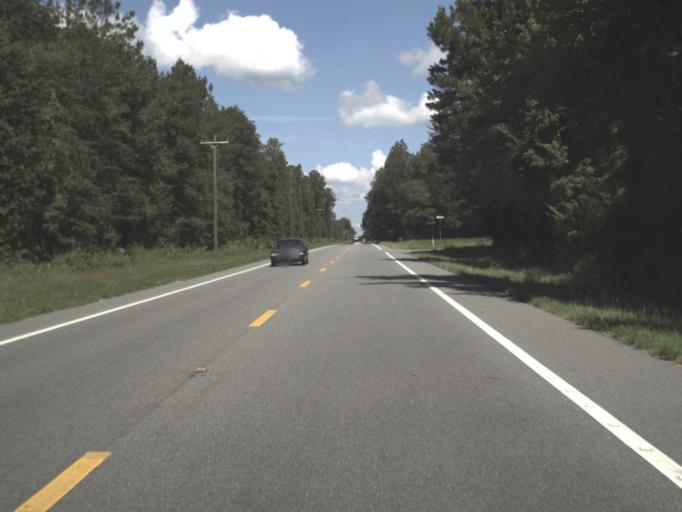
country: US
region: Florida
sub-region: Putnam County
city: Interlachen
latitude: 29.7052
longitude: -81.7795
